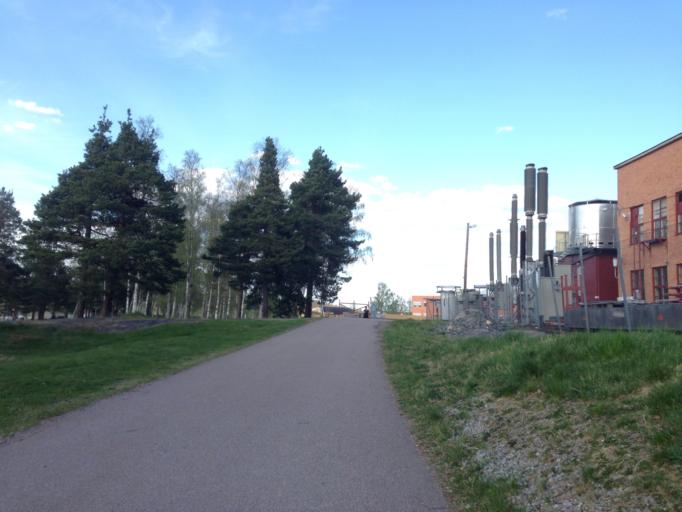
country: SE
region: Dalarna
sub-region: Ludvika Kommun
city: Ludvika
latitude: 60.1469
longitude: 15.1680
